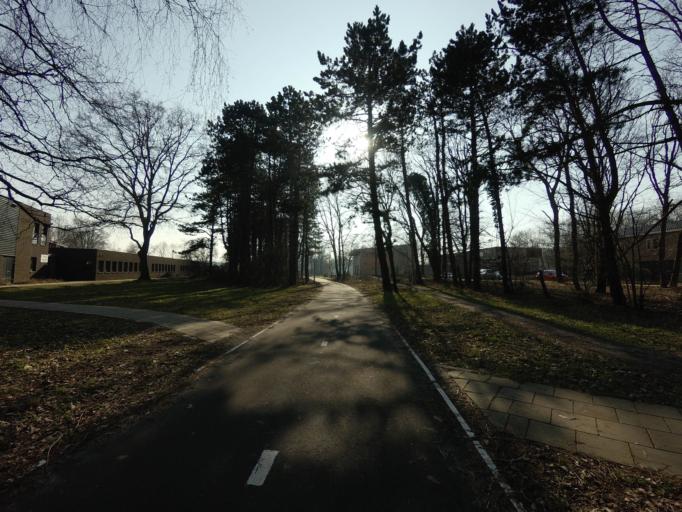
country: NL
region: North Holland
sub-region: Gemeente Velsen
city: Velsen-Zuid
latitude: 52.4405
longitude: 4.6324
